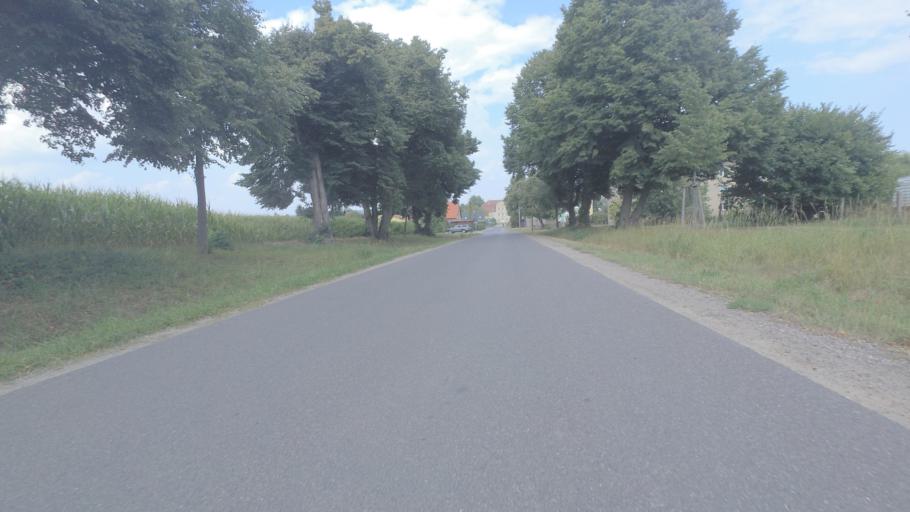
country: DE
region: Mecklenburg-Vorpommern
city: Neukalen
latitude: 53.7669
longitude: 12.8327
